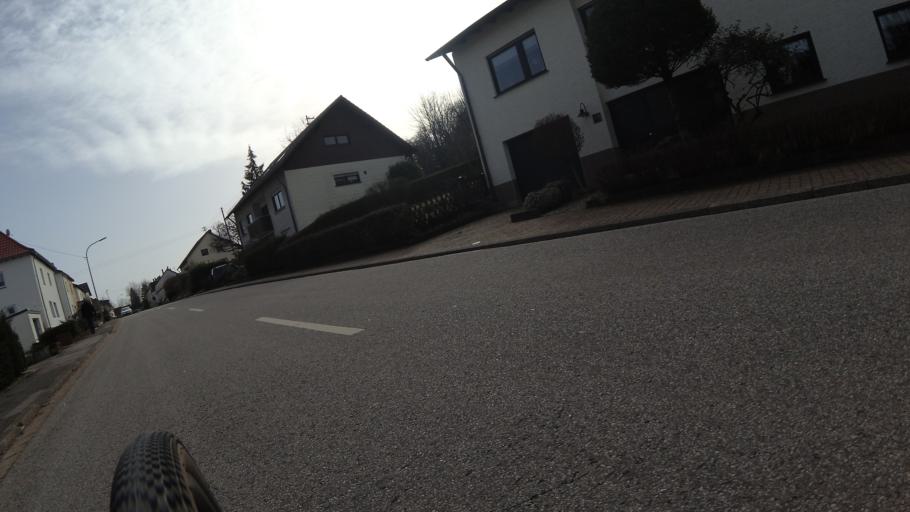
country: DE
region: Saarland
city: Uberherrn
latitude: 49.2661
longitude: 6.6891
